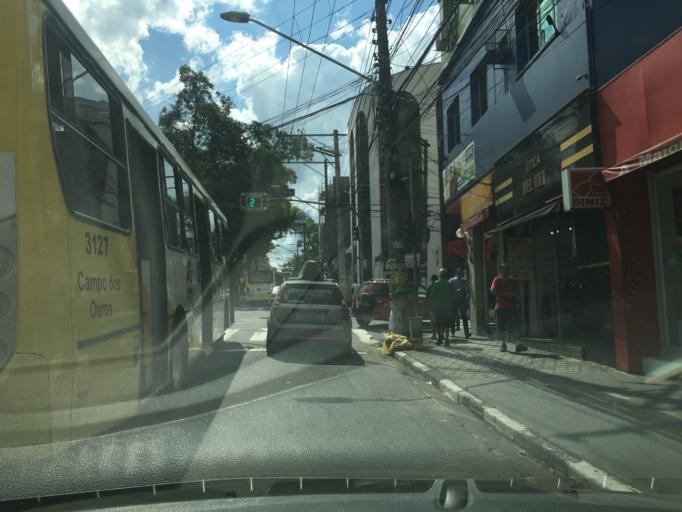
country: BR
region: Sao Paulo
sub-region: Guarulhos
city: Guarulhos
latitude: -23.4687
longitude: -46.5270
